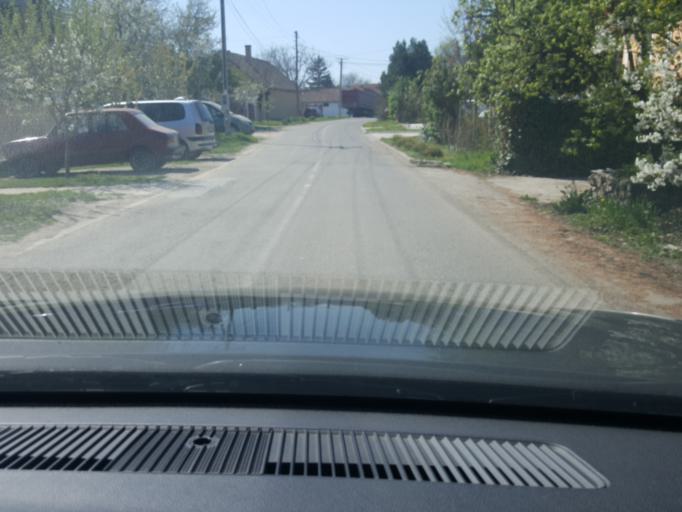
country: RS
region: Autonomna Pokrajina Vojvodina
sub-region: Zapadnobacki Okrug
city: Sombor
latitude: 45.7711
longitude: 19.0897
